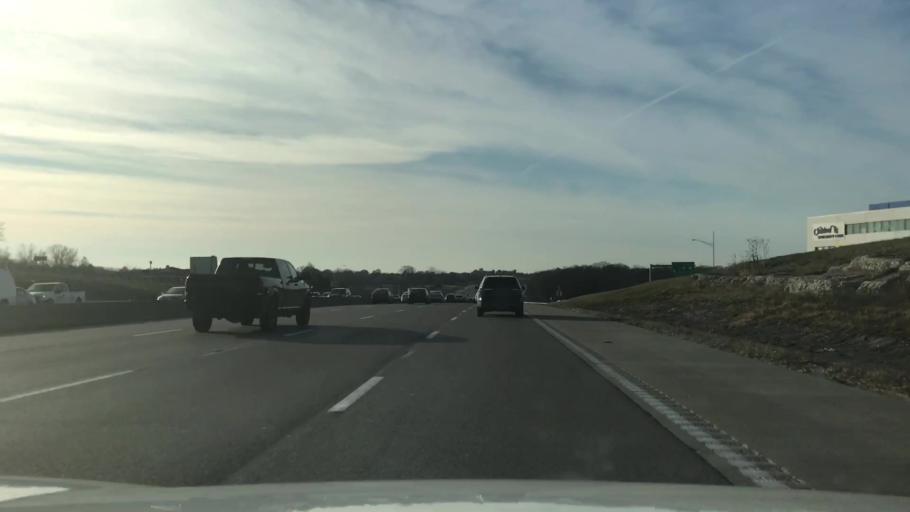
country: US
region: Missouri
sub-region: Saint Louis County
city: Town and Country
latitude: 38.6388
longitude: -90.4820
